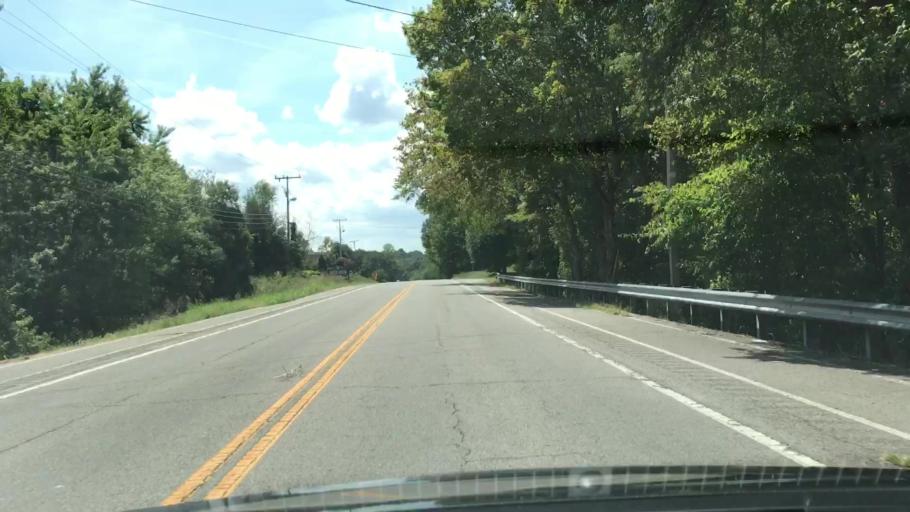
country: US
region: Tennessee
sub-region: Sumner County
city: White House
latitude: 36.4941
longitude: -86.6416
